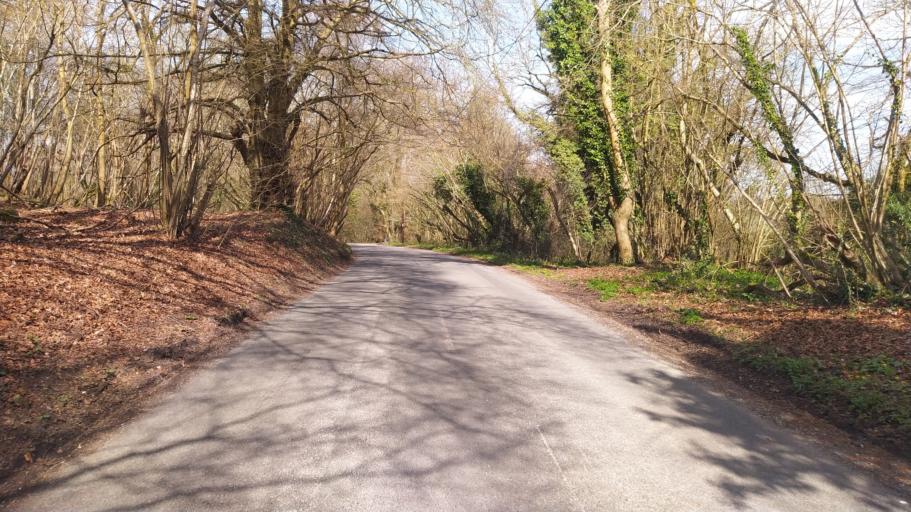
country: GB
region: England
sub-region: Hampshire
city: Four Marks
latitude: 51.0641
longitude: -1.1078
